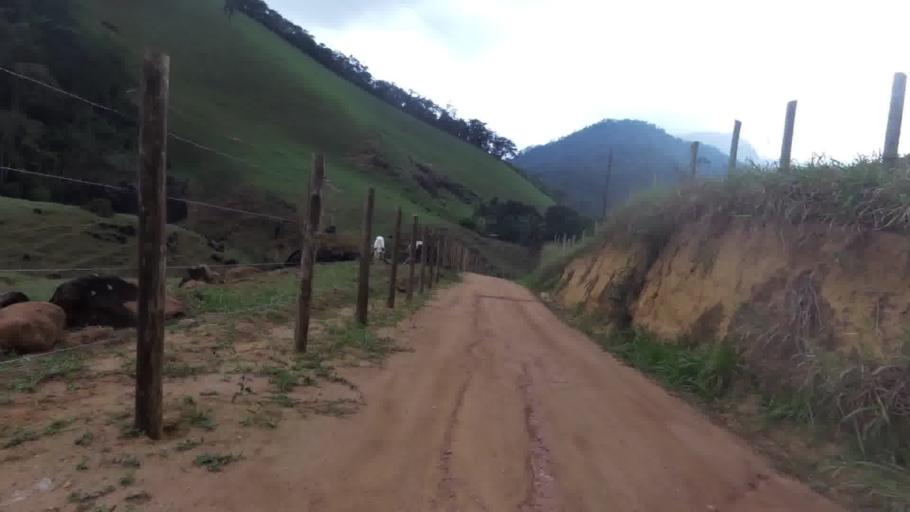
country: BR
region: Espirito Santo
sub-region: Alfredo Chaves
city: Alfredo Chaves
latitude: -20.6266
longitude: -40.7518
